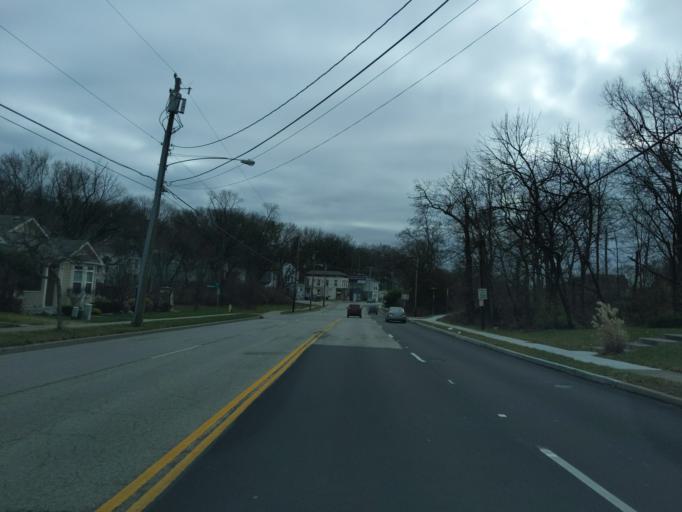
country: US
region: Ohio
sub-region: Hamilton County
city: Finneytown
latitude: 39.1732
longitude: -84.5475
